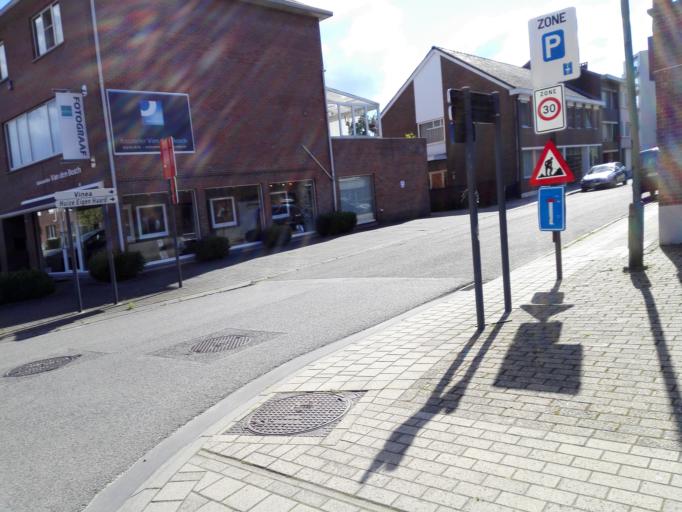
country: BE
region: Flanders
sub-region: Provincie Vlaams-Brabant
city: Aarschot
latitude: 50.9933
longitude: 4.8428
